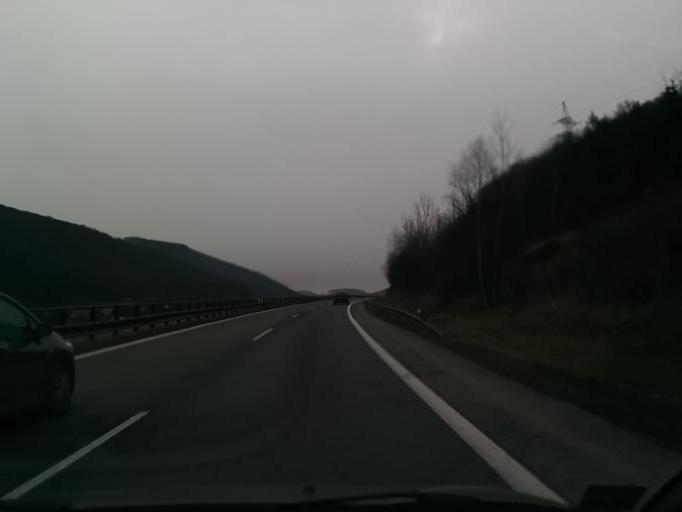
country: SK
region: Banskobystricky
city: Ziar nad Hronom
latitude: 48.5806
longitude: 18.9808
